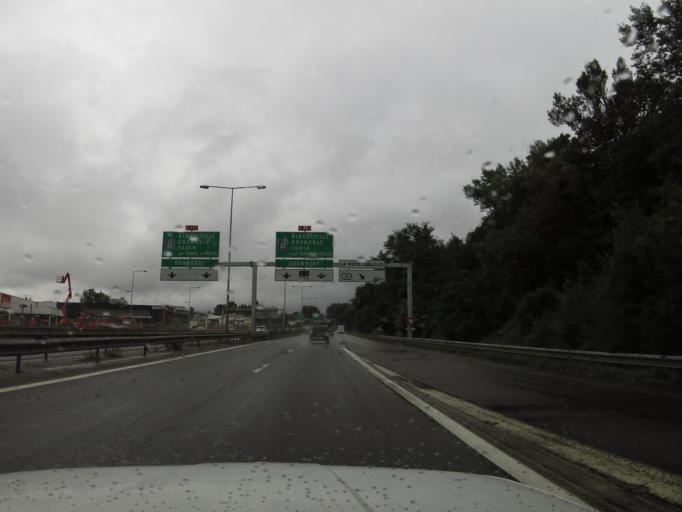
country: FR
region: Rhone-Alpes
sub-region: Departement de la Savoie
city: La Motte-Servolex
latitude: 45.6004
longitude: 5.8923
